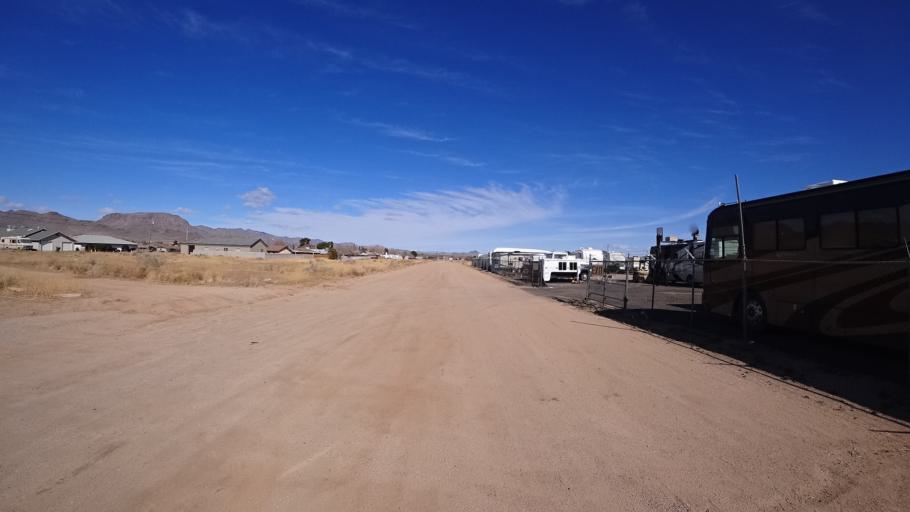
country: US
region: Arizona
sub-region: Mohave County
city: New Kingman-Butler
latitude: 35.2253
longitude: -114.0174
